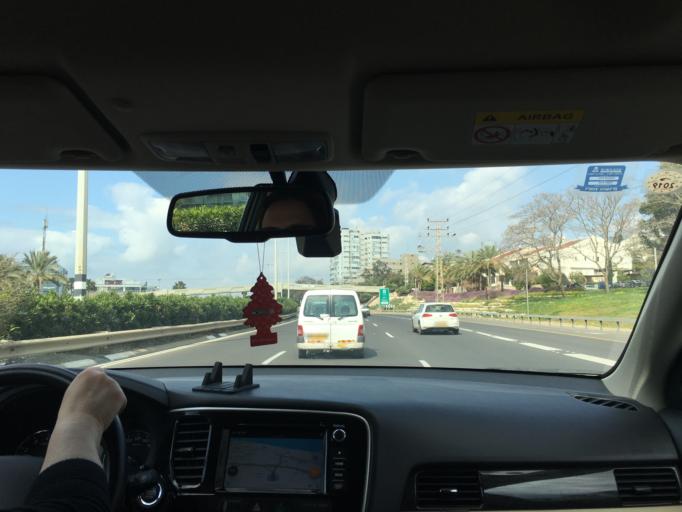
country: IL
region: Tel Aviv
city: Herzliyya
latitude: 32.1635
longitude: 34.8129
